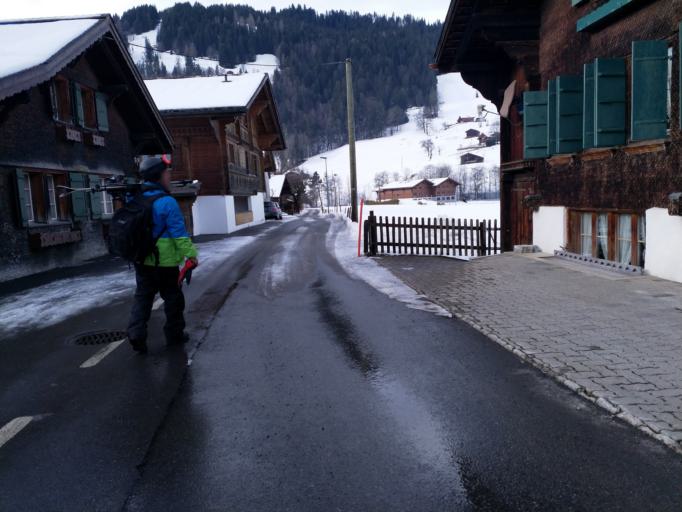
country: CH
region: Bern
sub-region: Obersimmental-Saanen District
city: Gstaad
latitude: 46.4703
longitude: 7.2839
